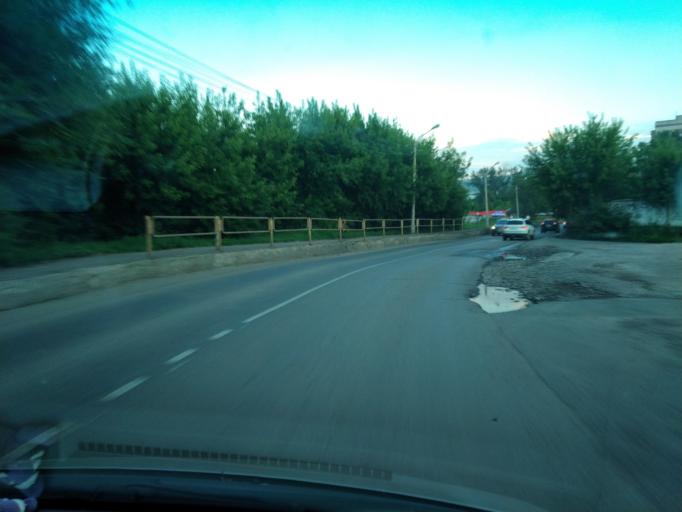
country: RU
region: Krasnoyarskiy
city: Krasnoyarsk
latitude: 55.9855
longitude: 92.8711
